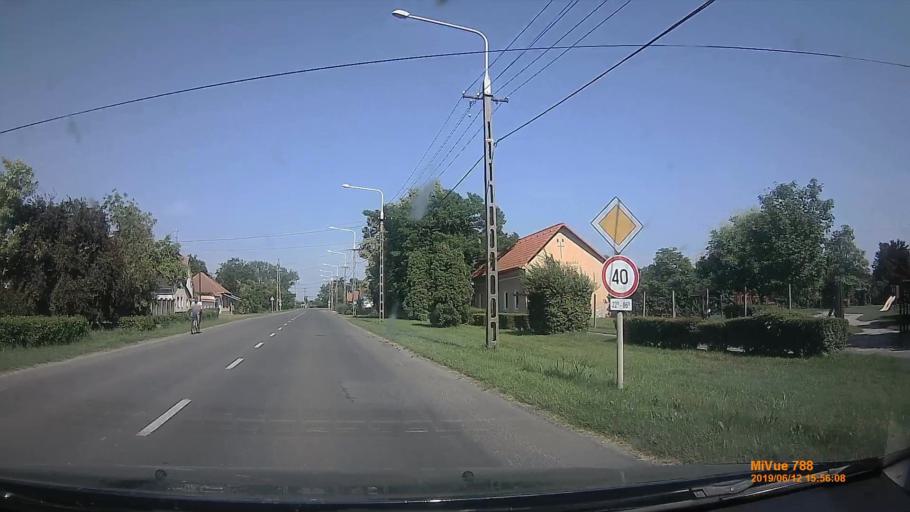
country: HU
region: Csongrad
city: Apatfalva
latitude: 46.1699
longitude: 20.6162
